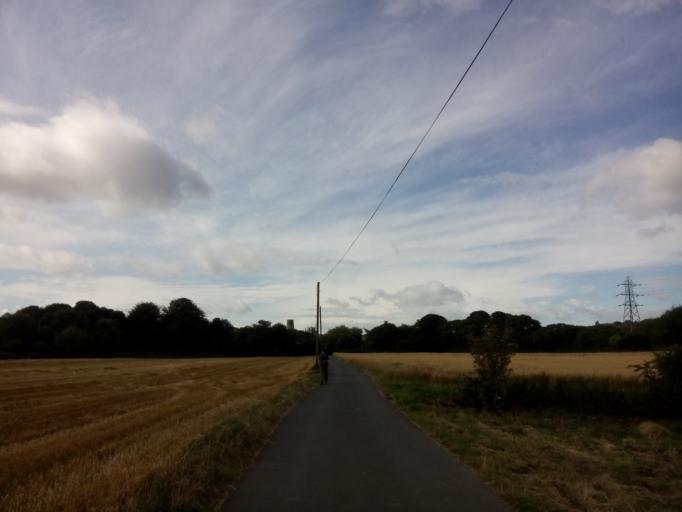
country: GB
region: England
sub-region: County Durham
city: Durham
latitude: 54.7865
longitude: -1.5656
